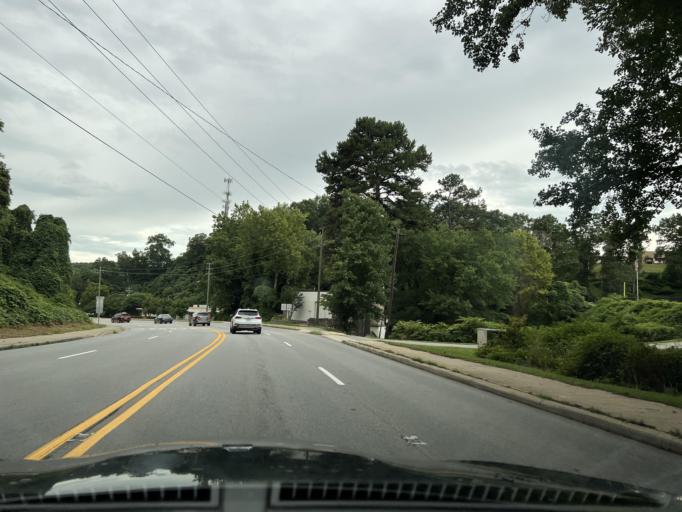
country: US
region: North Carolina
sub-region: Buncombe County
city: Asheville
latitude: 35.5712
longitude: -82.5507
